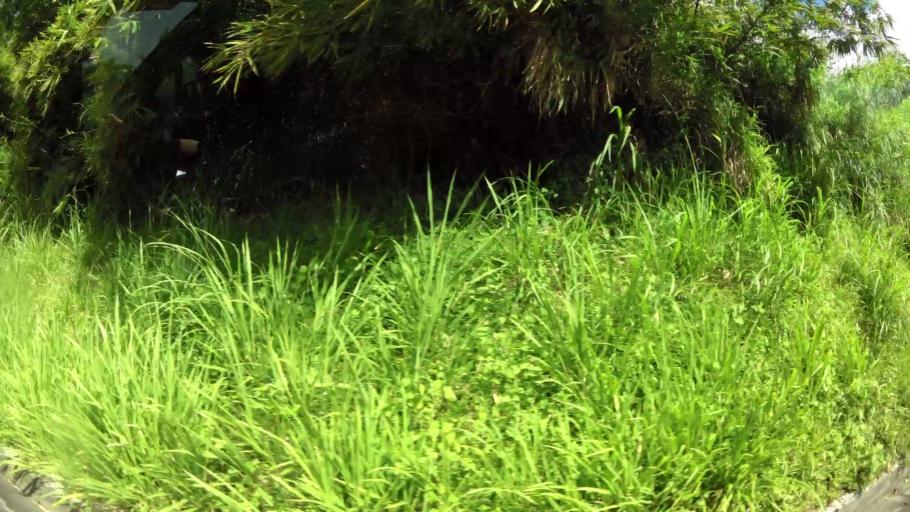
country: MQ
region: Martinique
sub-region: Martinique
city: Le Morne-Rouge
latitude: 14.7615
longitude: -61.1534
